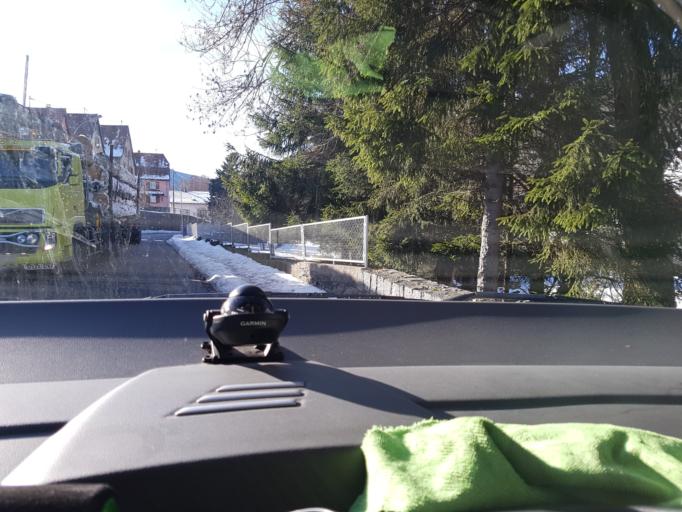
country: FR
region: Alsace
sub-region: Departement du Haut-Rhin
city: Metzeral
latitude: 47.9955
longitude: 7.0727
